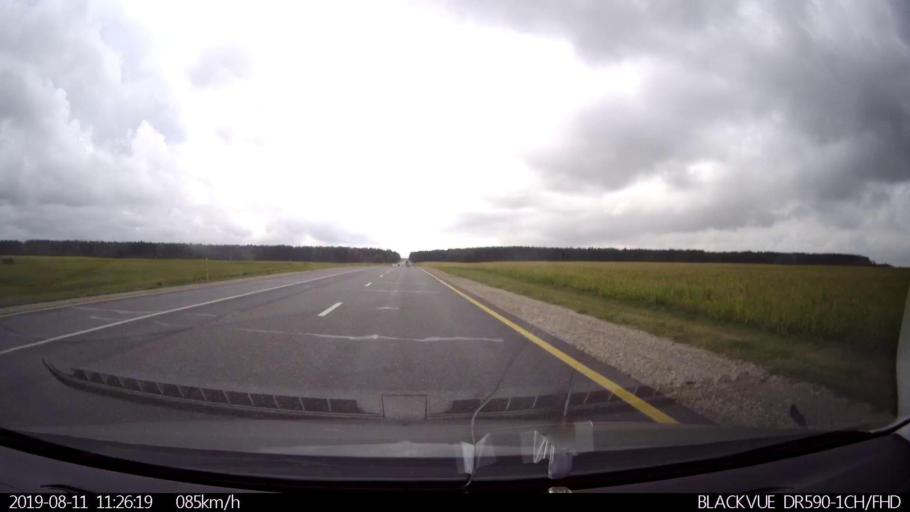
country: RU
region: Ulyanovsk
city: Krasnyy Gulyay
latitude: 54.1071
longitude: 48.2356
